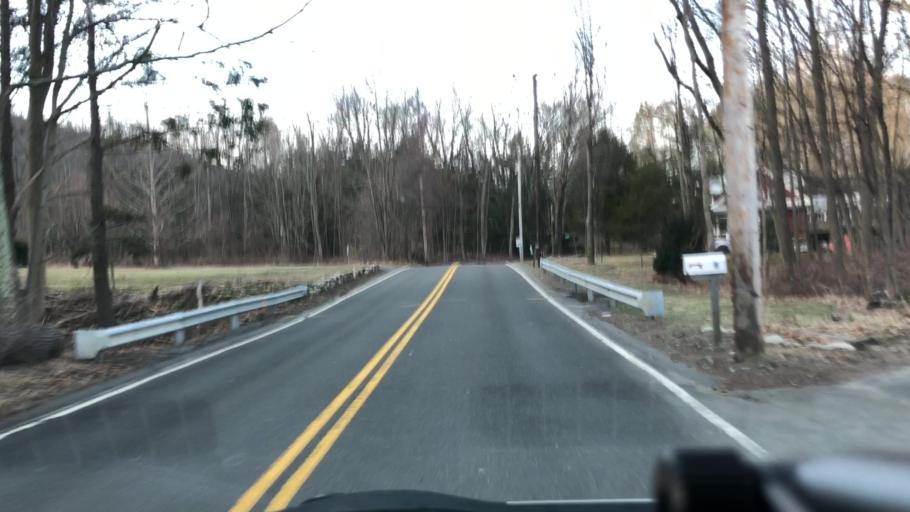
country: US
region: Massachusetts
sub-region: Hampshire County
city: Easthampton
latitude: 42.2488
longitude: -72.6537
